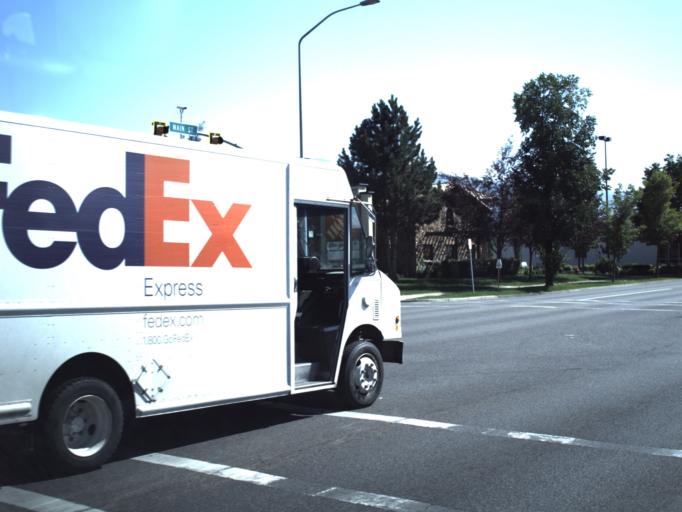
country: US
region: Utah
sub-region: Cache County
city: Logan
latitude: 41.7545
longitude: -111.8345
